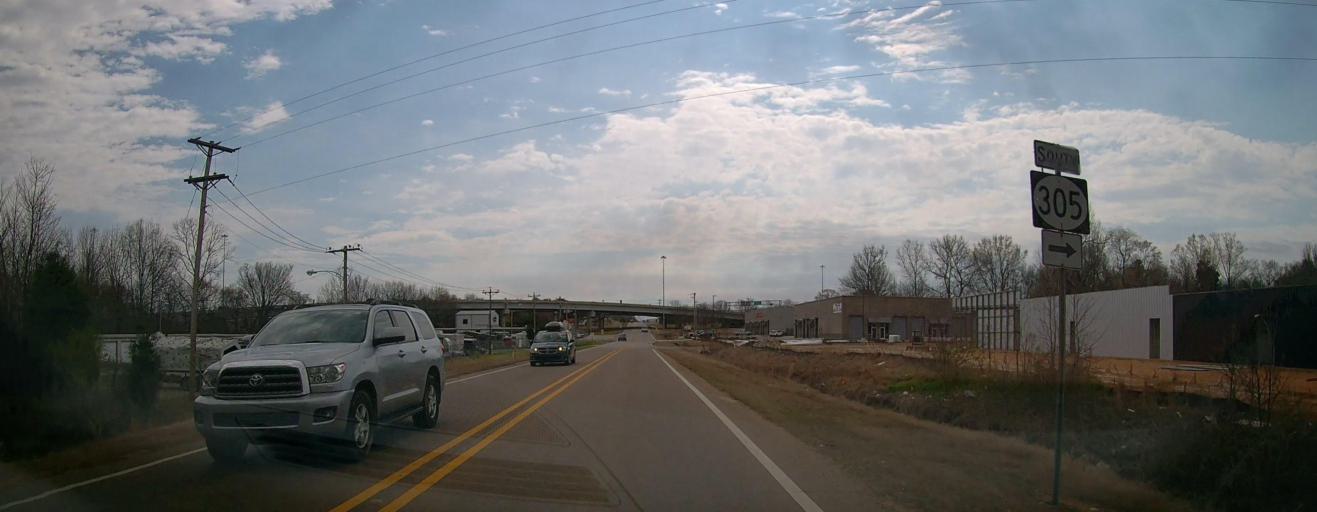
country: US
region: Mississippi
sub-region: De Soto County
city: Olive Branch
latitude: 34.9676
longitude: -89.8334
